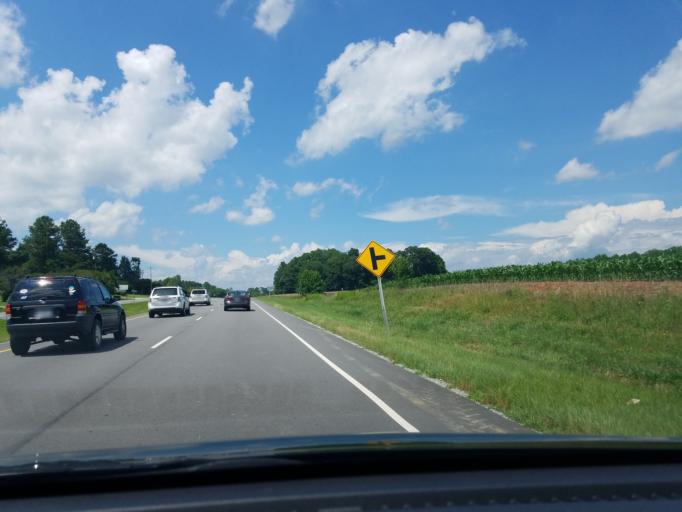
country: US
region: North Carolina
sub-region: Durham County
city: Gorman
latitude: 36.1440
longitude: -78.9052
